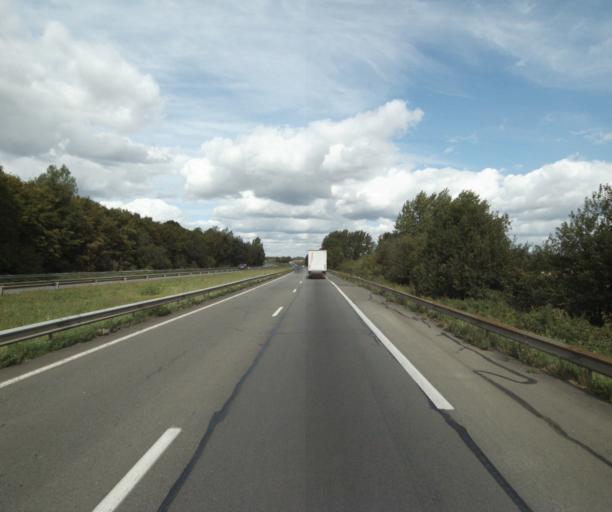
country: FR
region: Nord-Pas-de-Calais
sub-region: Departement du Nord
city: Genech
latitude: 50.5125
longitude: 3.2105
